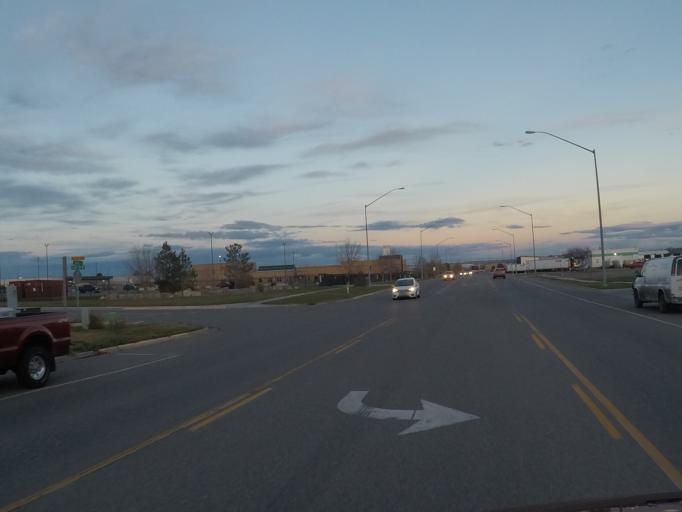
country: US
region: Montana
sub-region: Yellowstone County
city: Billings
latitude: 45.7445
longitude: -108.5932
